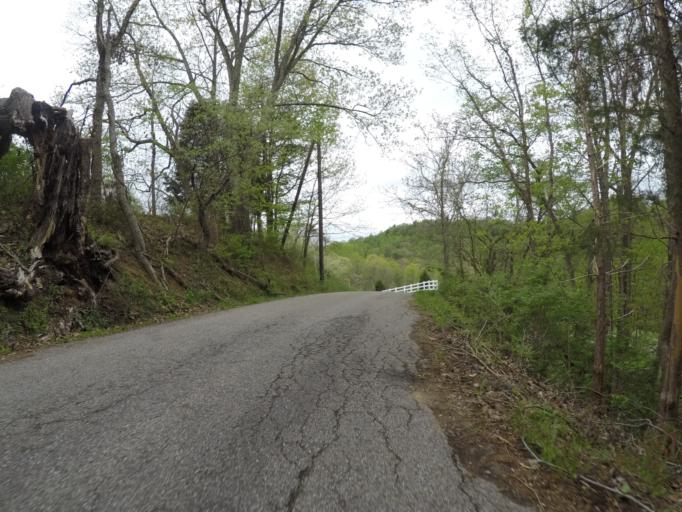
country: US
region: West Virginia
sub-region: Cabell County
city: Barboursville
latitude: 38.3926
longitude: -82.2506
